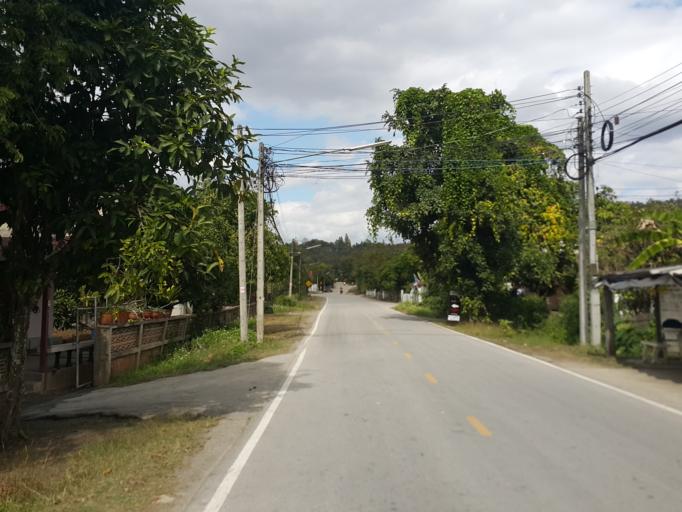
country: TH
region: Chiang Mai
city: San Sai
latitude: 18.8610
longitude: 99.1411
